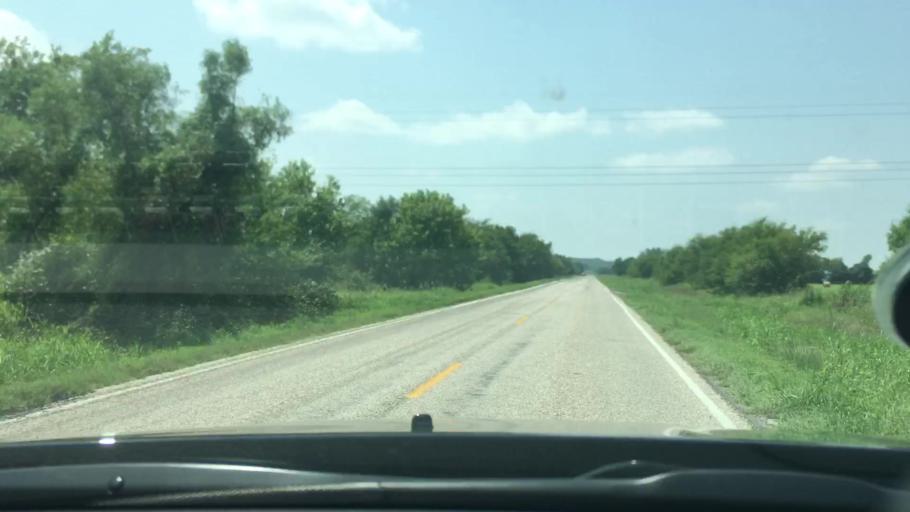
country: US
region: Oklahoma
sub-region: Johnston County
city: Tishomingo
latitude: 34.3761
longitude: -96.4746
